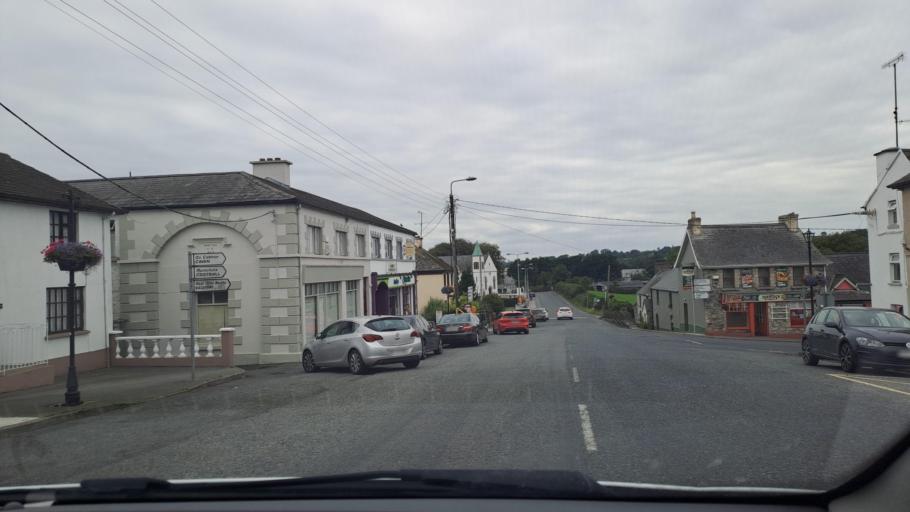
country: IE
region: Ulster
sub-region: An Cabhan
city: Bailieborough
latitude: 53.9953
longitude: -6.8986
